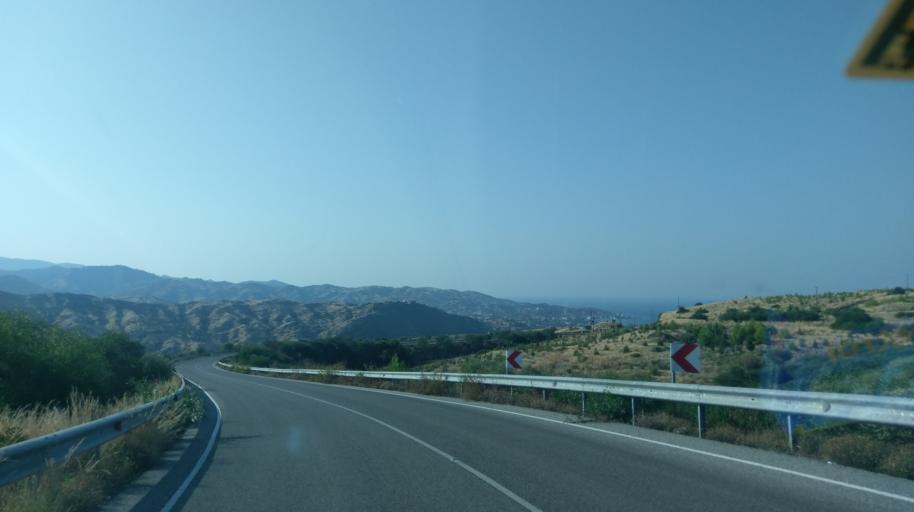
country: CY
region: Lefkosia
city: Kato Pyrgos
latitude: 35.1662
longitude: 32.7117
